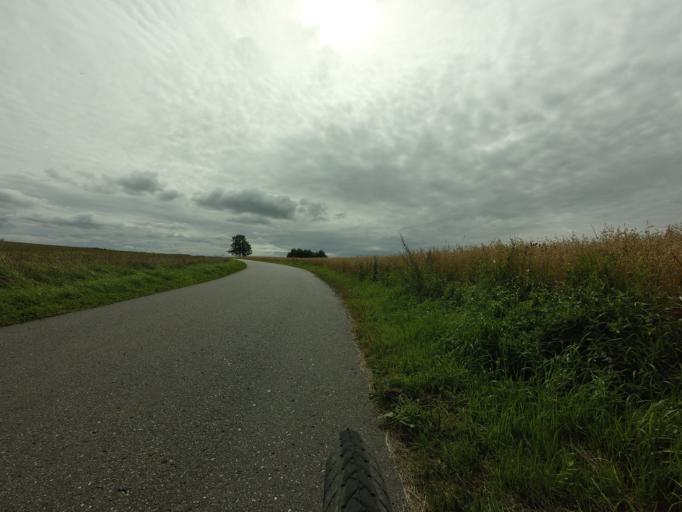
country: DK
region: Central Jutland
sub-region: Syddjurs Kommune
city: Ryomgard
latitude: 56.3993
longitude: 10.5473
